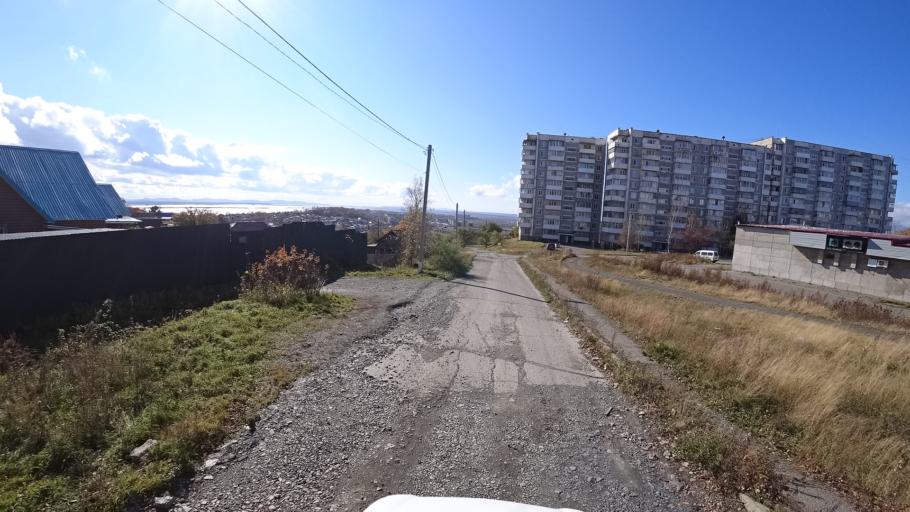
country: RU
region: Khabarovsk Krai
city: Amursk
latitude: 50.2406
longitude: 136.9194
